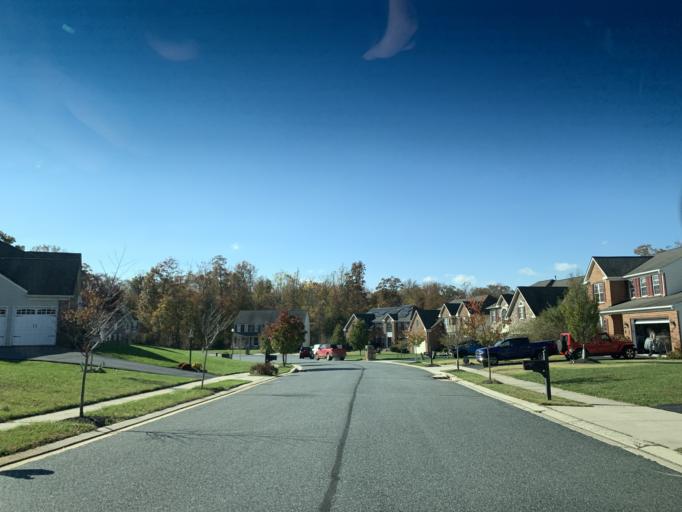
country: US
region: Maryland
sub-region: Harford County
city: Joppatowne
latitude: 39.4420
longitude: -76.3346
